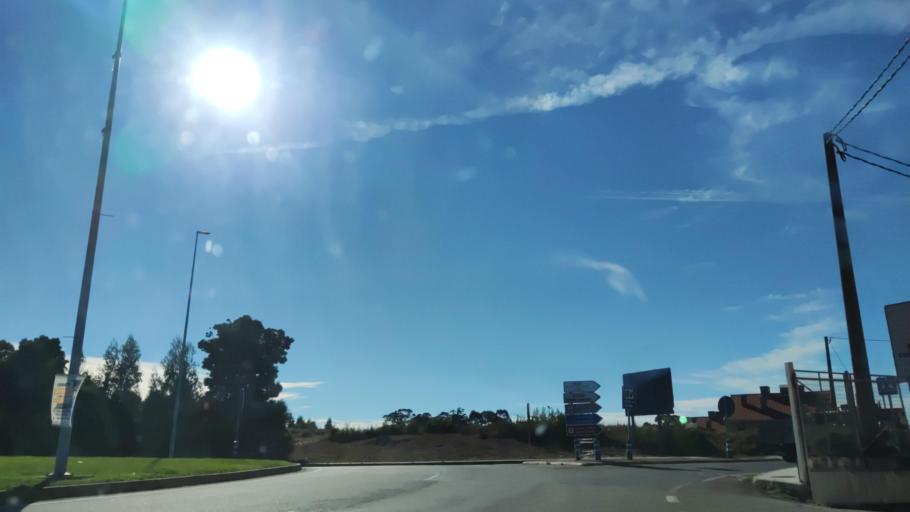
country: ES
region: Galicia
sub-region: Provincia da Coruna
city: Boiro
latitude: 42.5707
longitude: -8.9985
